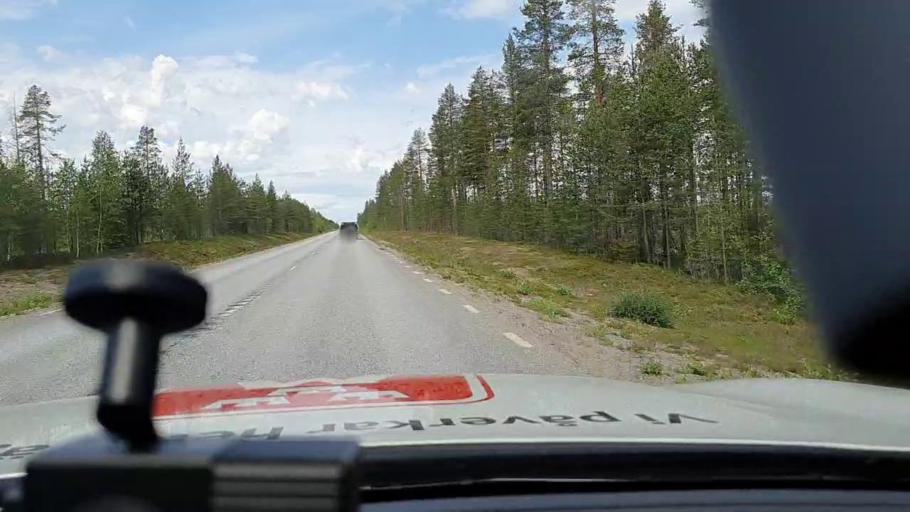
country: SE
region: Norrbotten
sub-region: Jokkmokks Kommun
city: Jokkmokk
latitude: 66.5205
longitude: 20.2148
